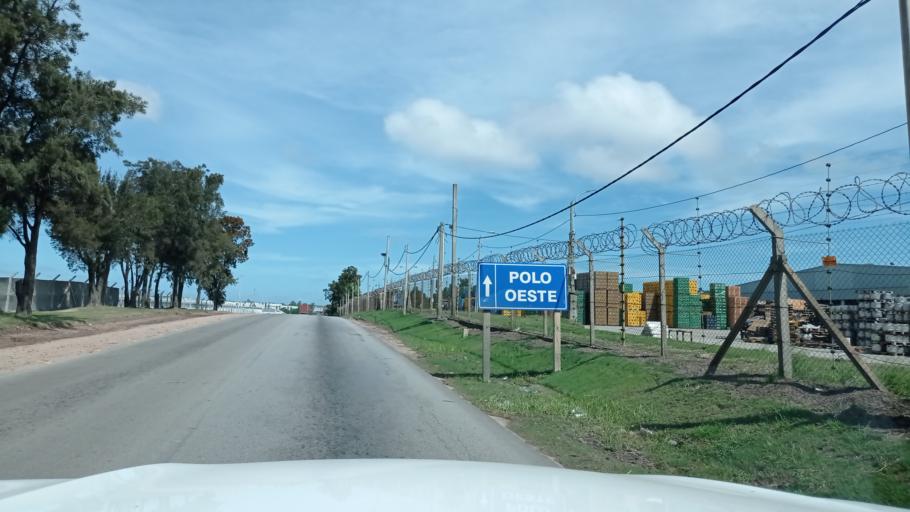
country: UY
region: Montevideo
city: Pajas Blancas
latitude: -34.8543
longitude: -56.2900
